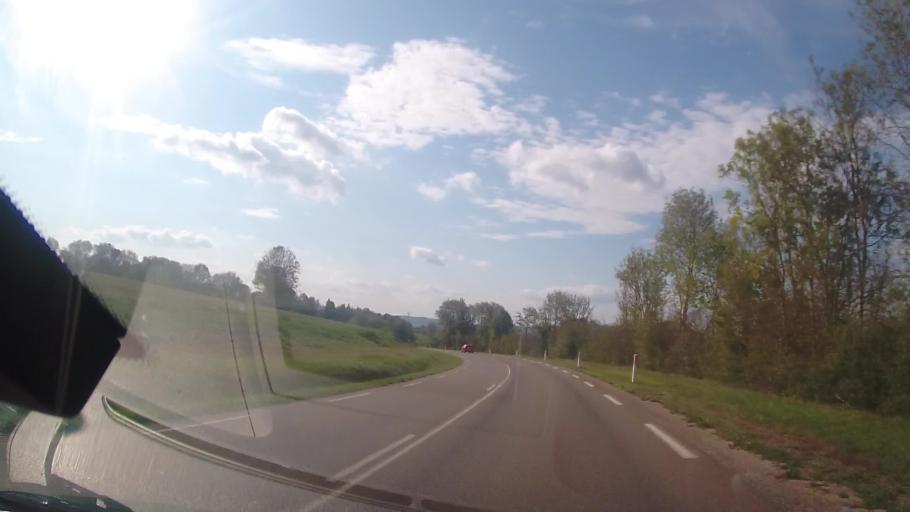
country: FR
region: Franche-Comte
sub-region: Departement du Jura
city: Clairvaux-les-Lacs
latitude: 46.5837
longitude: 5.7690
